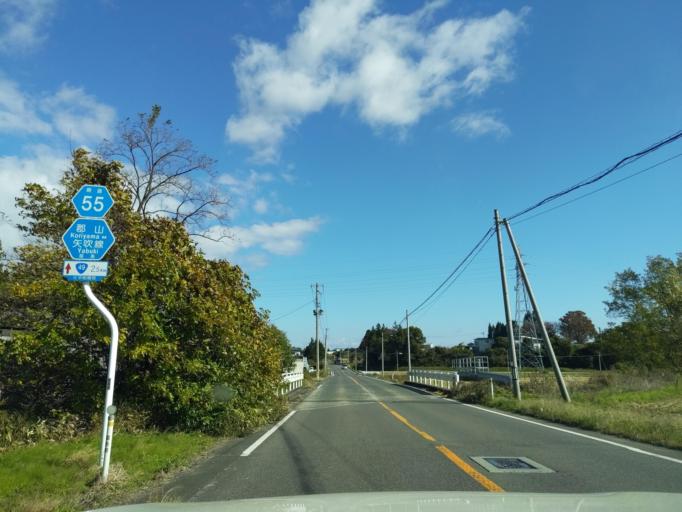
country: JP
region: Fukushima
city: Koriyama
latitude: 37.4292
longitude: 140.3272
